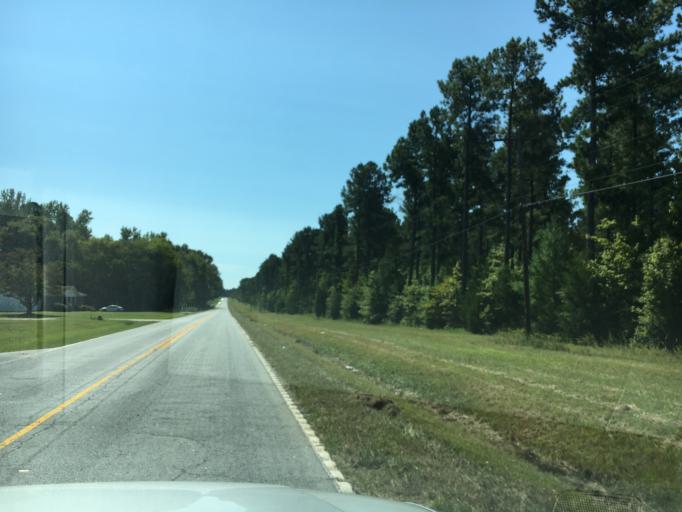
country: US
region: South Carolina
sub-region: Laurens County
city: Clinton
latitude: 34.4468
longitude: -81.8727
